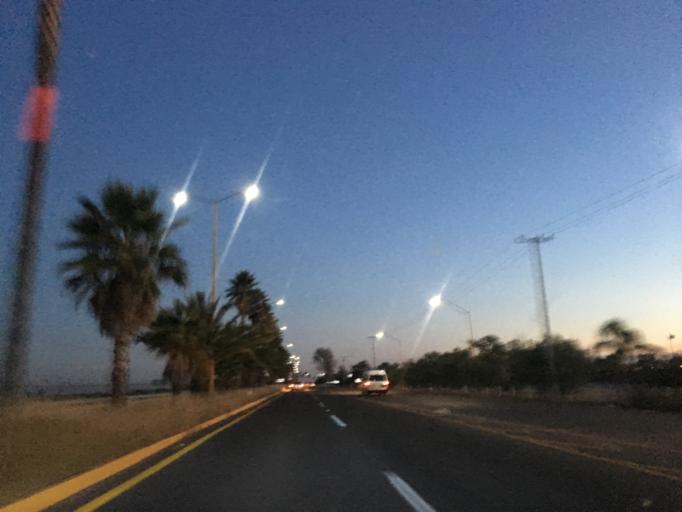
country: MX
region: Aguascalientes
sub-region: Aguascalientes
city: Penuelas (El Cienegal)
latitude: 21.7190
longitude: -102.3102
